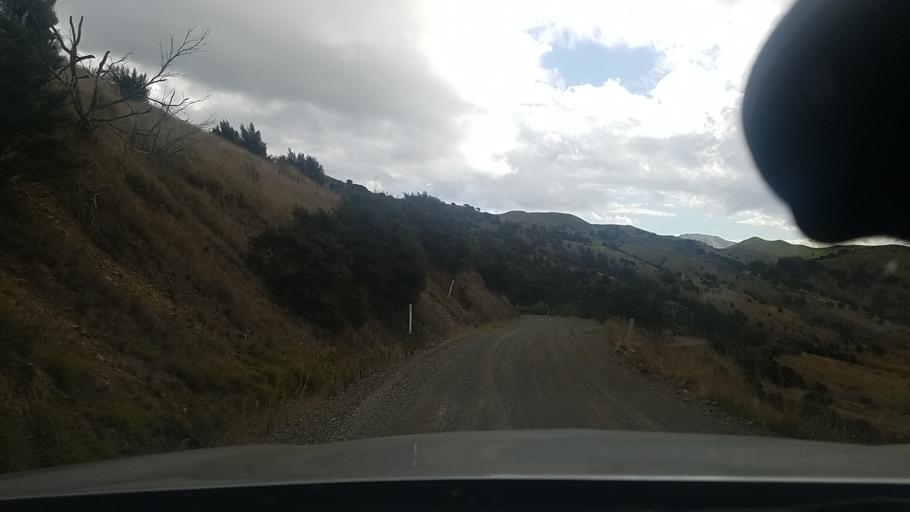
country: NZ
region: Marlborough
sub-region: Marlborough District
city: Blenheim
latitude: -41.5865
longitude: 174.0725
